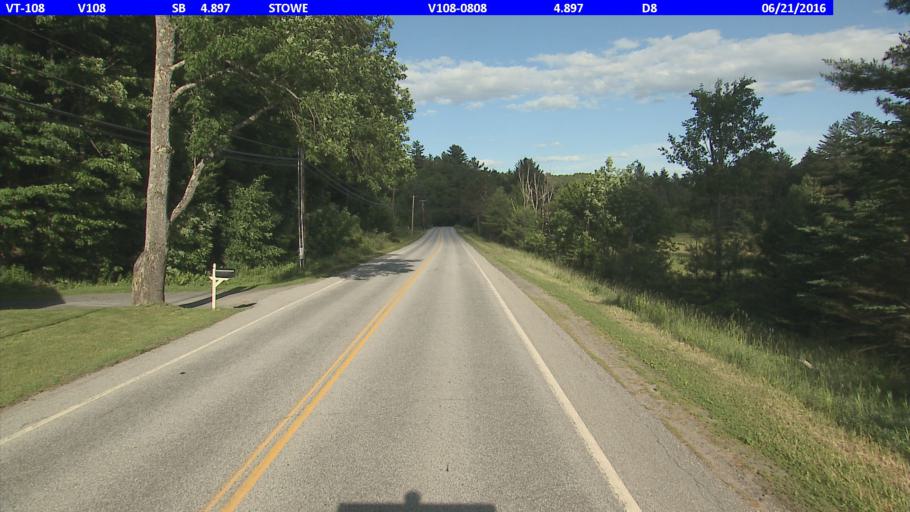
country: US
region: Vermont
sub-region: Lamoille County
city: Morristown
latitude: 44.5014
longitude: -72.7523
